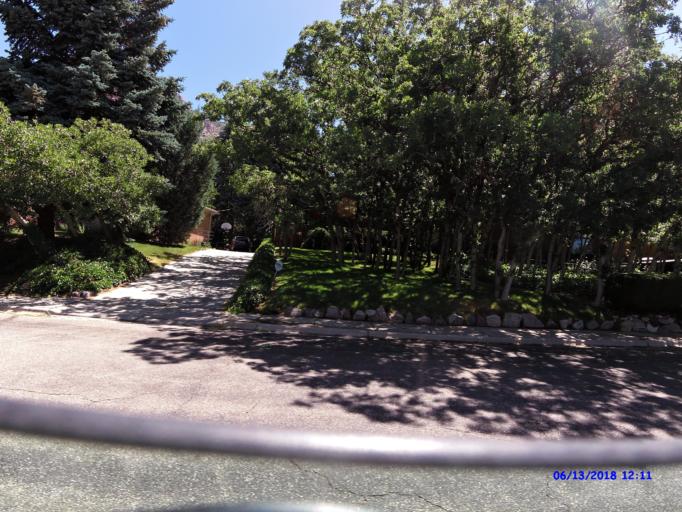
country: US
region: Utah
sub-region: Weber County
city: Ogden
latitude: 41.2141
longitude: -111.9296
